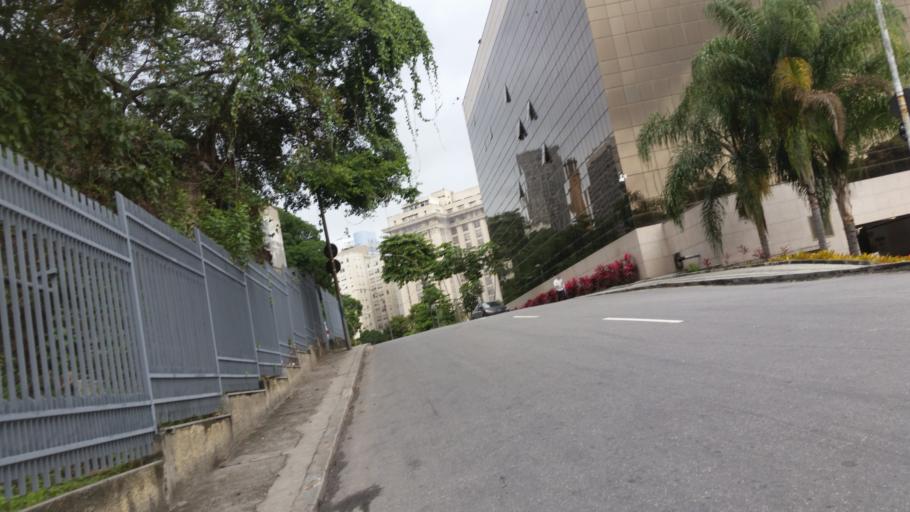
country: BR
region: Rio de Janeiro
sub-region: Rio De Janeiro
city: Rio de Janeiro
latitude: -22.9060
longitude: -43.1709
